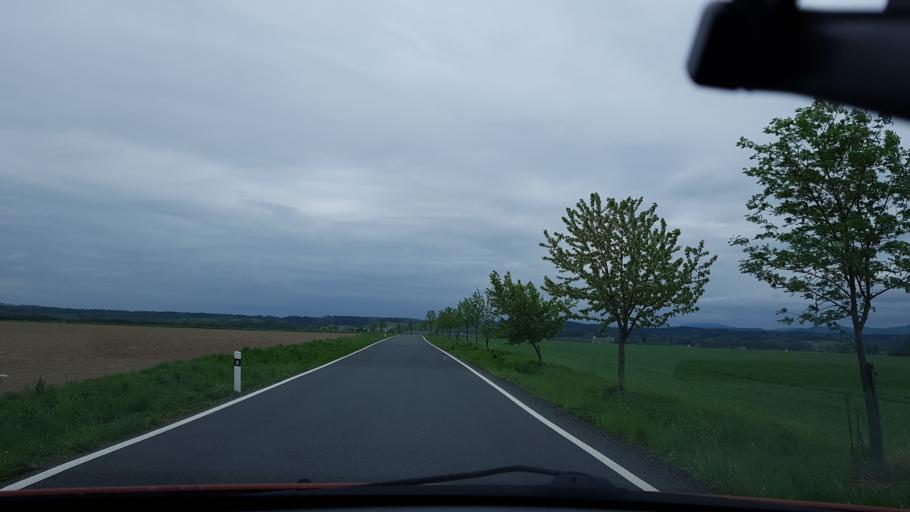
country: CZ
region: Olomoucky
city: Vidnava
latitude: 50.3808
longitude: 17.1546
